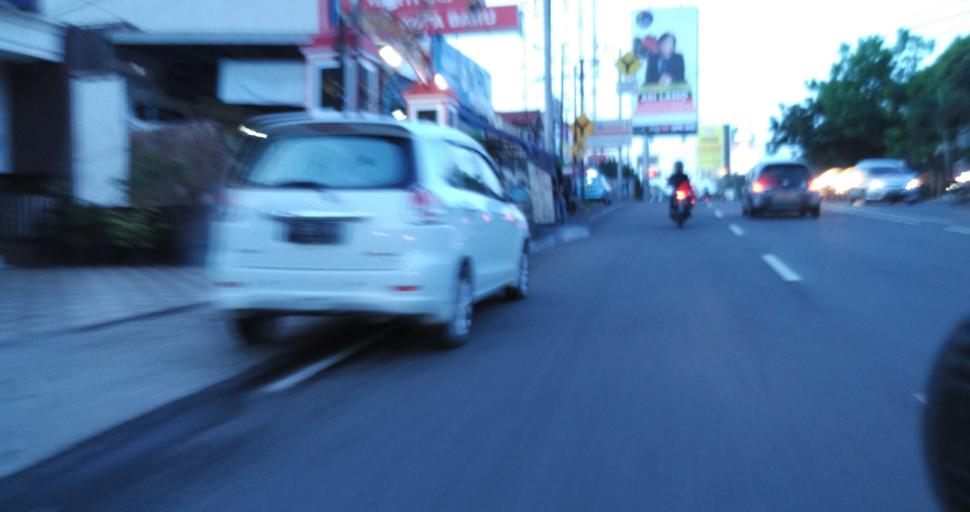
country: ID
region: Central Java
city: Semarang
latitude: -7.0451
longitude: 110.4213
